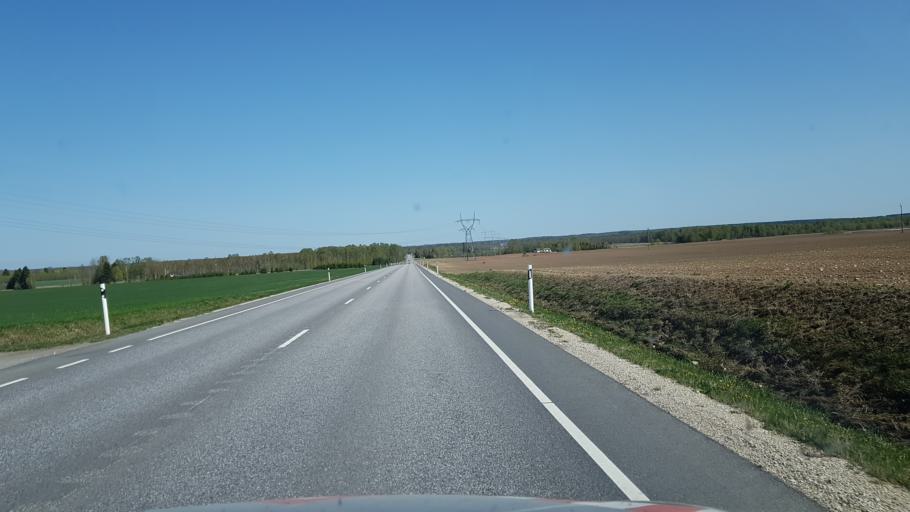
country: EE
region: Tartu
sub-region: Puhja vald
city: Puhja
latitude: 58.3461
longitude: 26.4127
